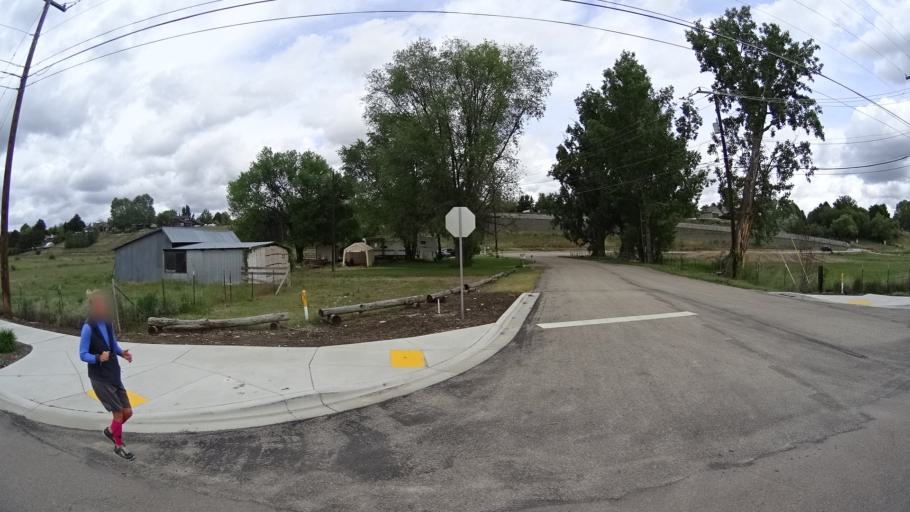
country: US
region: Idaho
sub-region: Ada County
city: Eagle
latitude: 43.6955
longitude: -116.3340
